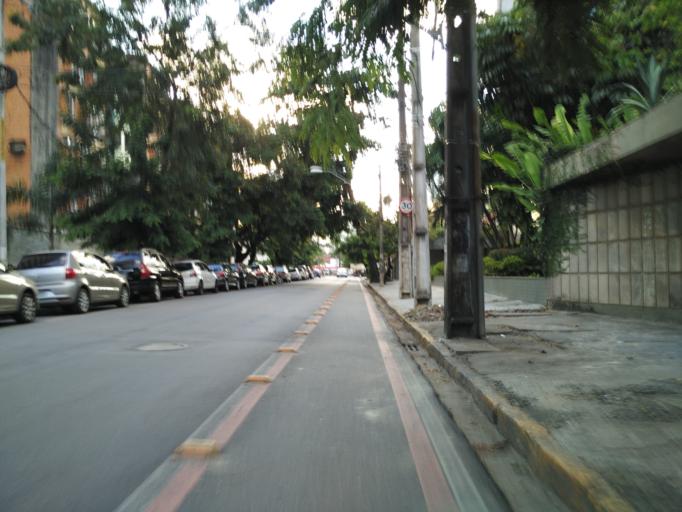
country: BR
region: Pernambuco
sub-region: Recife
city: Recife
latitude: -8.0328
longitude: -34.9089
